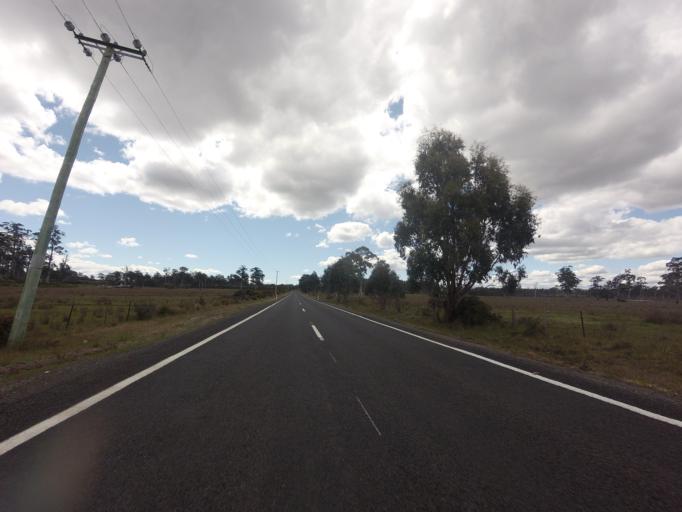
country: AU
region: Tasmania
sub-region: Northern Midlands
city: Evandale
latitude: -41.9860
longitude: 147.6702
